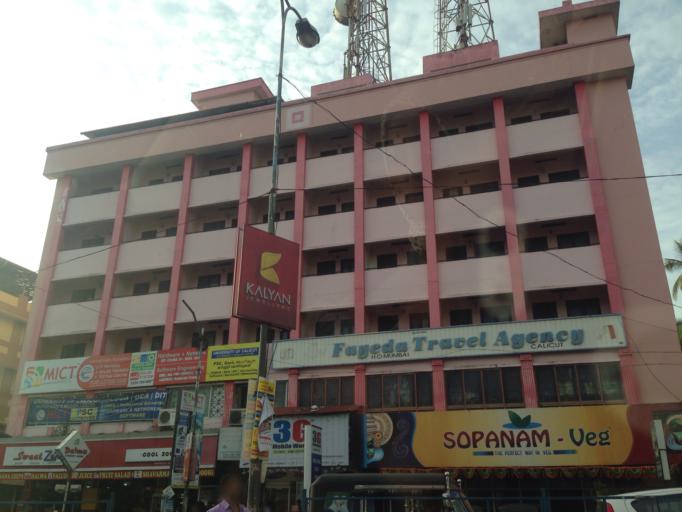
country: IN
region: Kerala
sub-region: Kozhikode
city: Kozhikode
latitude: 11.2593
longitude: 75.7851
